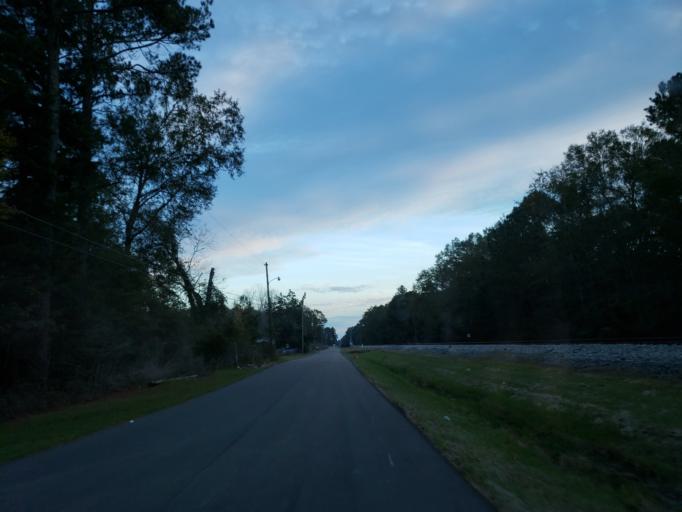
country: US
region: Mississippi
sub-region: Forrest County
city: Hattiesburg
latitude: 31.2772
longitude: -89.2542
